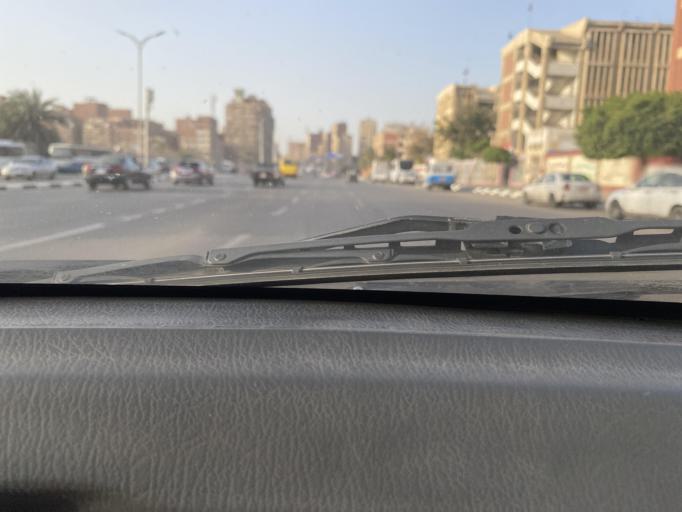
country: EG
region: Muhafazat al Qahirah
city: Cairo
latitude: 30.1158
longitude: 31.2964
